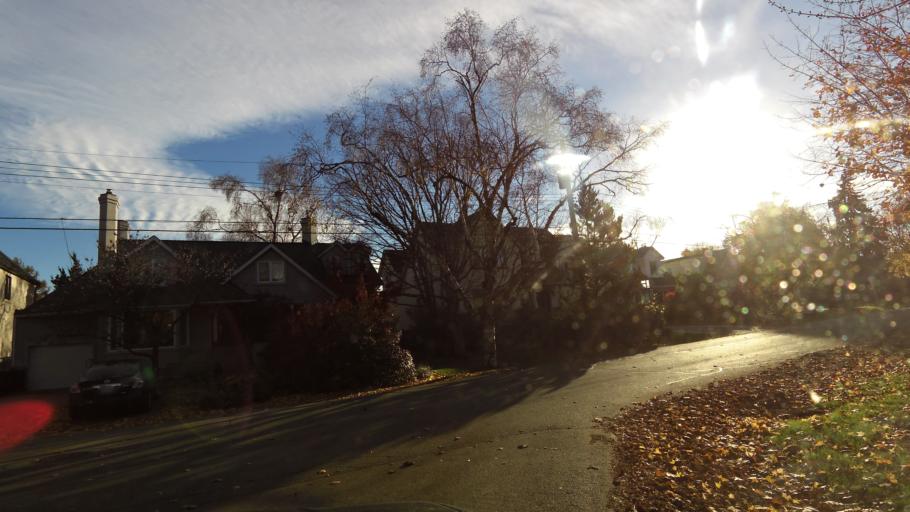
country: CA
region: Ontario
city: Etobicoke
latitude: 43.6426
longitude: -79.5177
